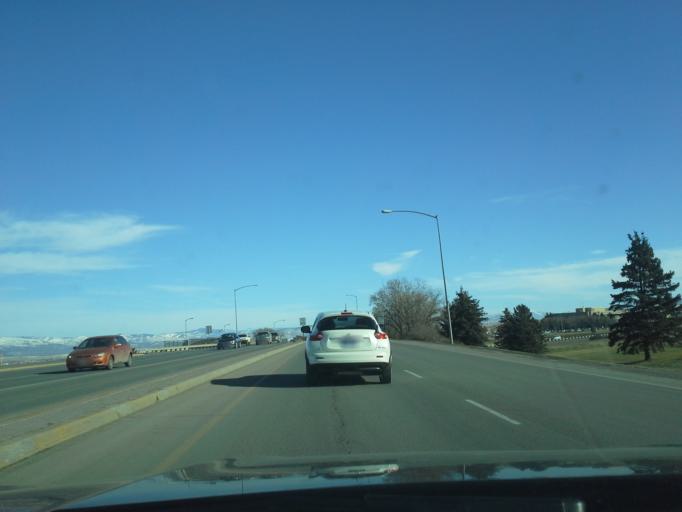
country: US
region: Montana
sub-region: Lewis and Clark County
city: Helena
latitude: 46.5912
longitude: -112.0009
